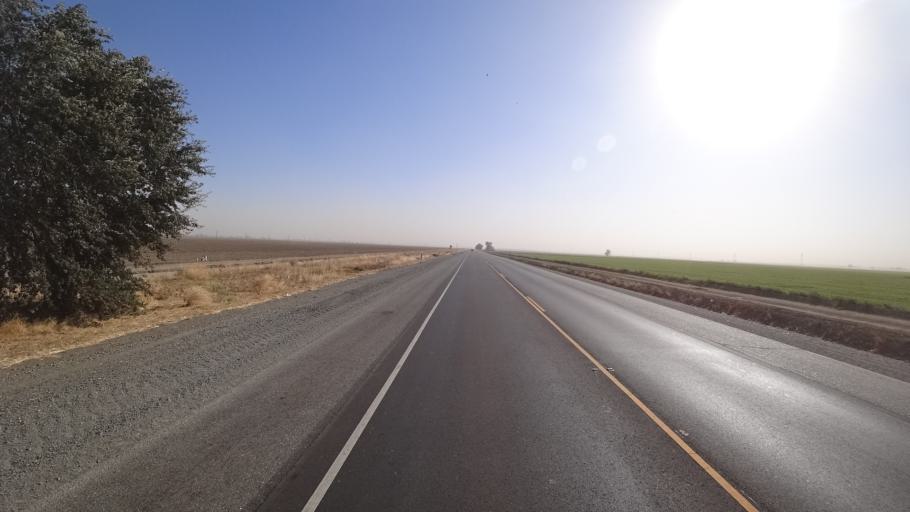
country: US
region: California
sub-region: Yolo County
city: Woodland
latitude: 38.7772
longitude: -121.7286
